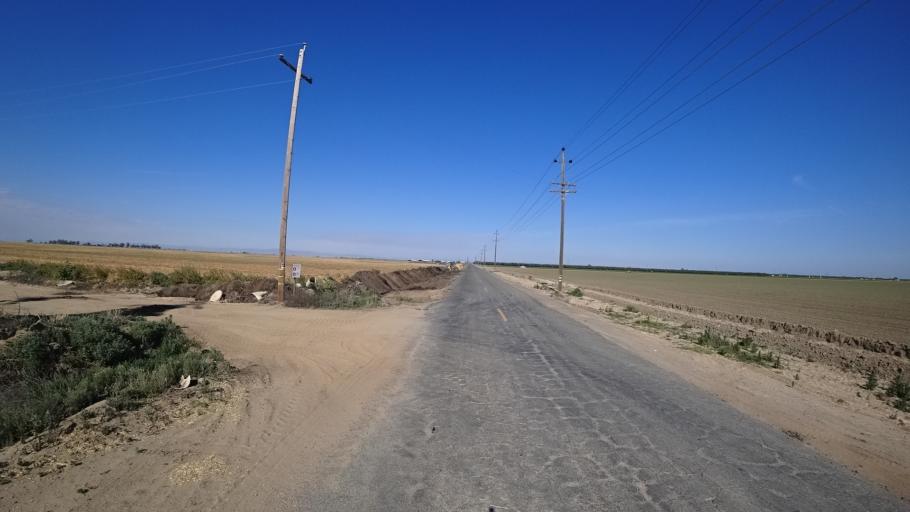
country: US
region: California
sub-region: Kings County
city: Armona
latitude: 36.2257
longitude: -119.6906
